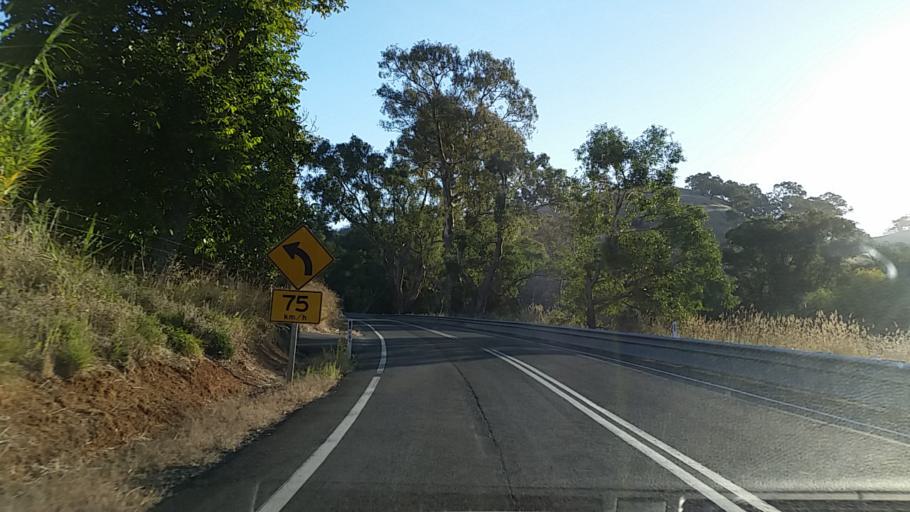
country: AU
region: South Australia
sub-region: Adelaide Hills
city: Gumeracha
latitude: -34.8302
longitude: 138.8504
